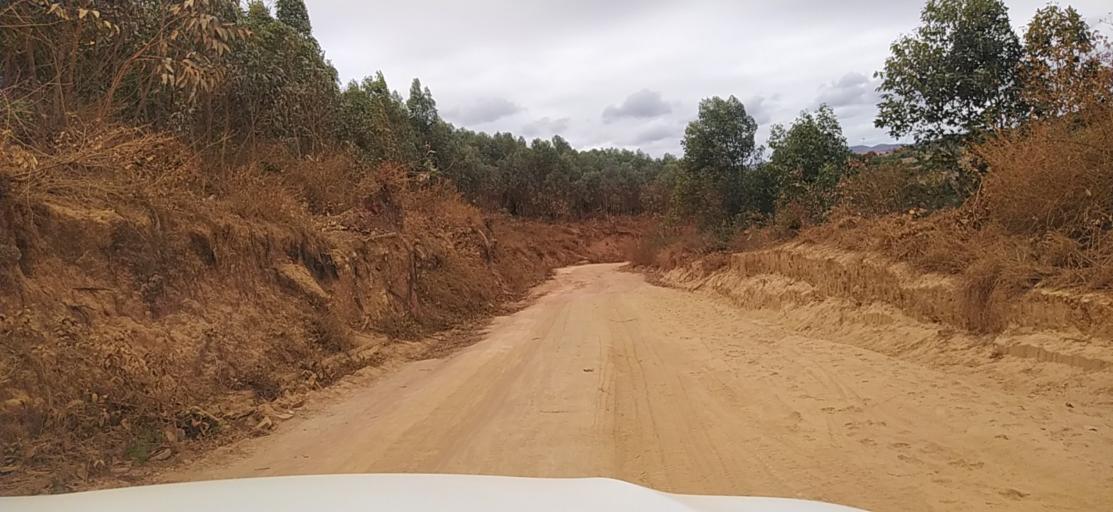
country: MG
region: Alaotra Mangoro
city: Ambatondrazaka
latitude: -18.0060
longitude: 48.2599
